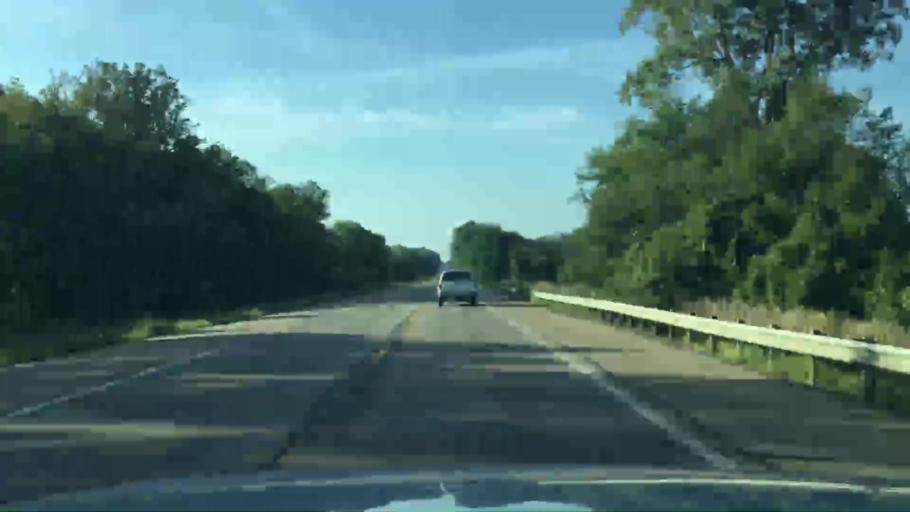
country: US
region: Michigan
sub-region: Jackson County
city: Vandercook Lake
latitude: 42.1002
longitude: -84.3639
